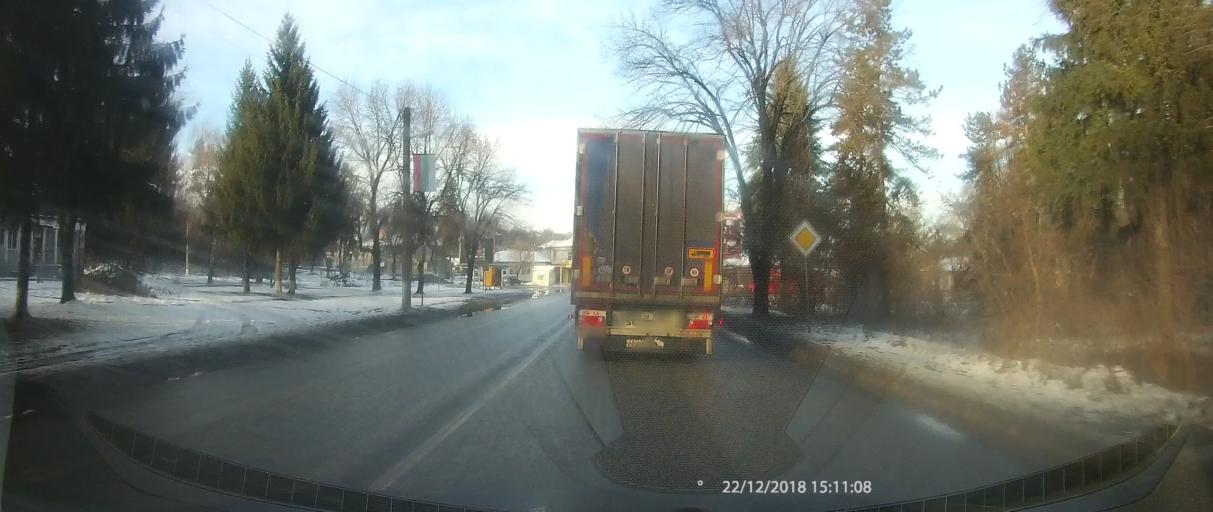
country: BG
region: Ruse
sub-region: Obshtina Borovo
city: Borovo
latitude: 43.5245
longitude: 25.7967
